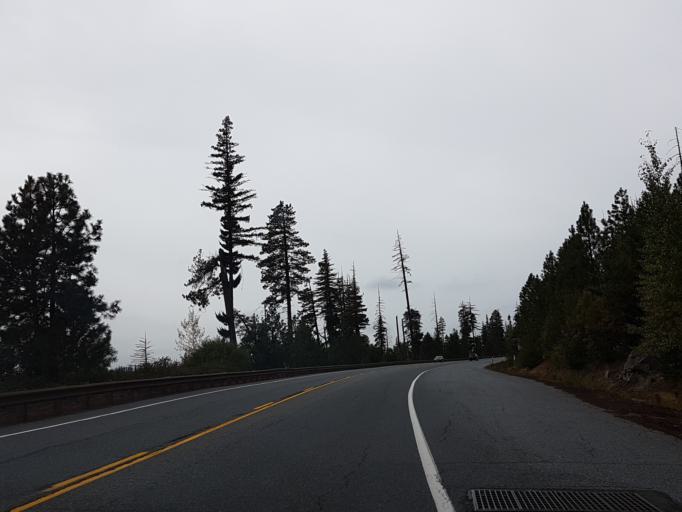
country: US
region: Oregon
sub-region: Deschutes County
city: Sisters
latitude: 44.4187
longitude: -121.7788
